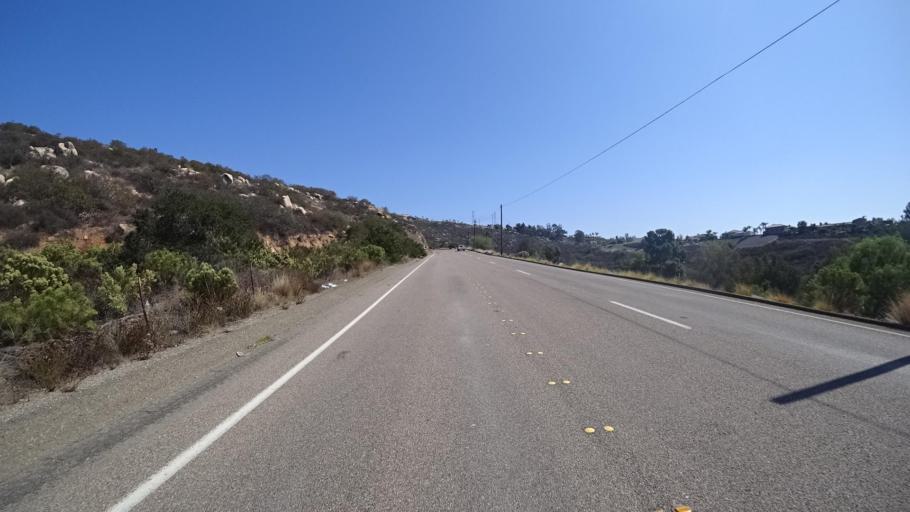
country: US
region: California
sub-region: San Diego County
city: Granite Hills
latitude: 32.8101
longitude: -116.8994
